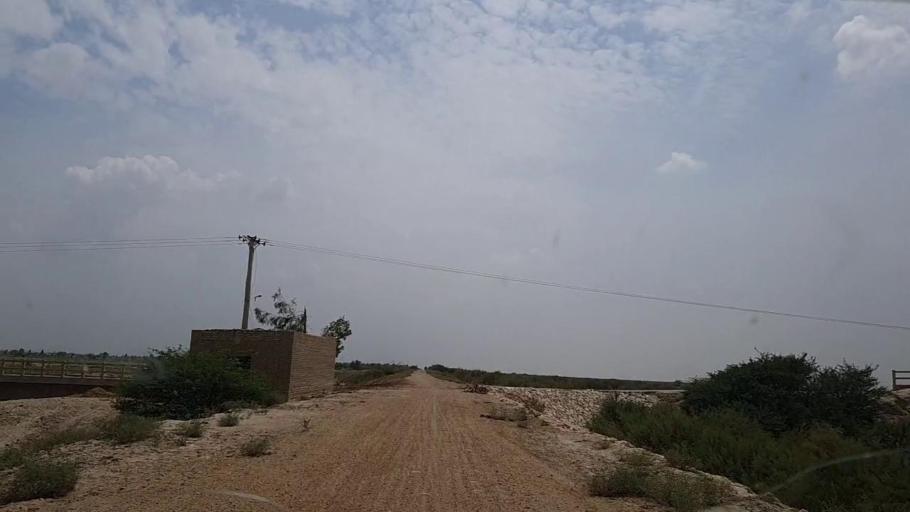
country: PK
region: Sindh
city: Phulji
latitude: 26.8212
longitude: 67.6124
